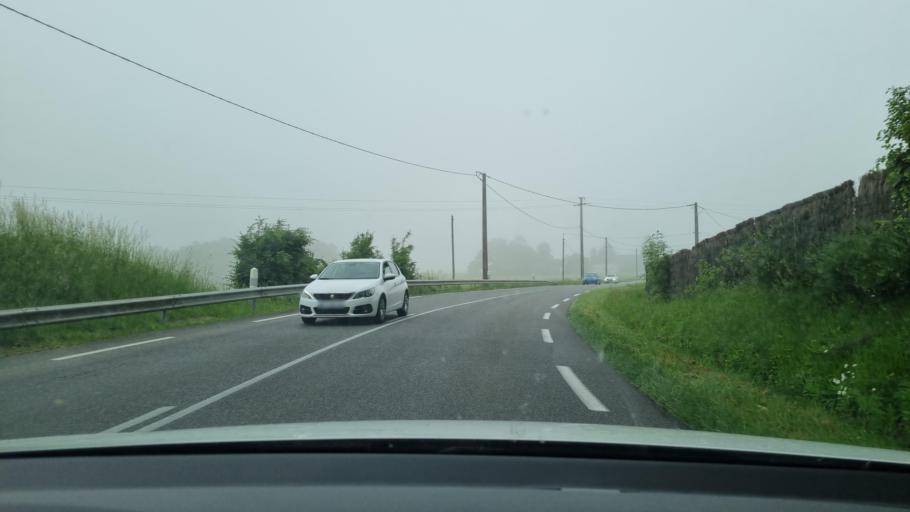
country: FR
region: Aquitaine
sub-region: Departement des Landes
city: Amou
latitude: 43.5270
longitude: -0.7033
